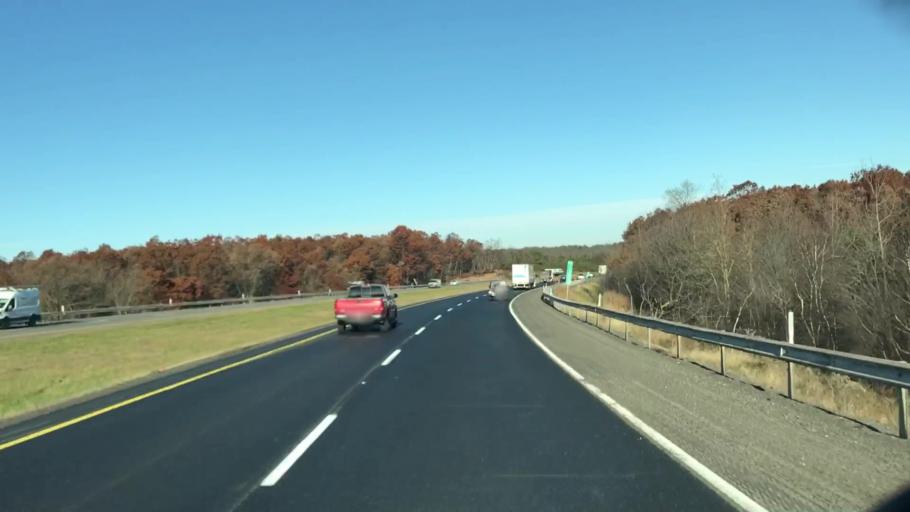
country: US
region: Pennsylvania
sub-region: Schuylkill County
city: McAdoo
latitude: 40.8932
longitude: -76.0264
